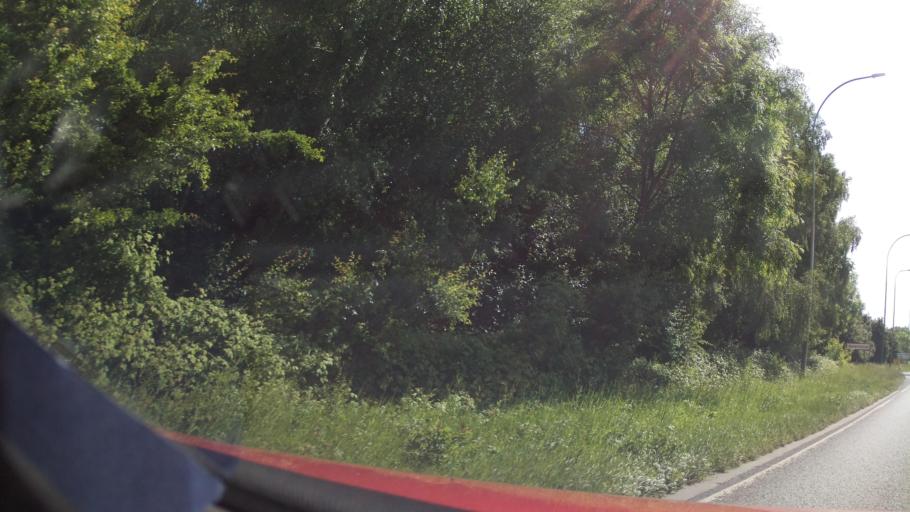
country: GB
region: England
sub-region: North Lincolnshire
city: Broughton
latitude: 53.5565
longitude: -0.5878
